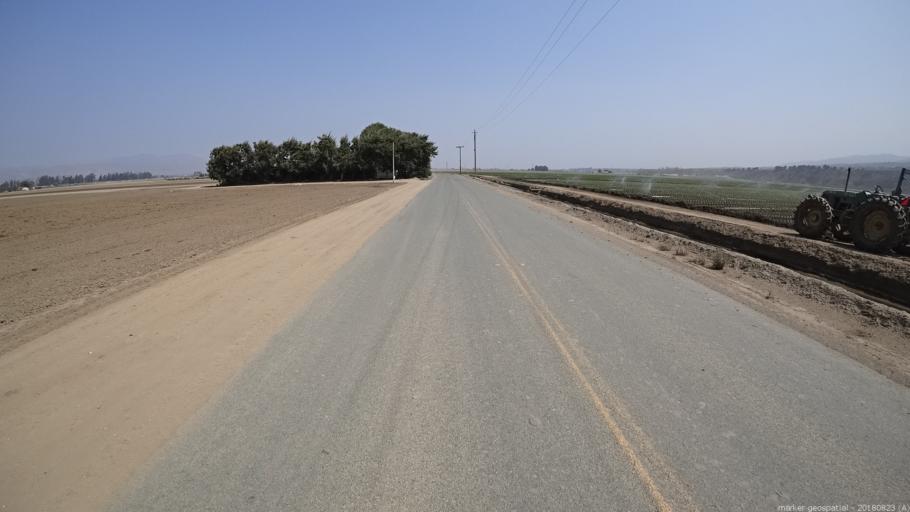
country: US
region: California
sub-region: Monterey County
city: Soledad
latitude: 36.4095
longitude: -121.3767
